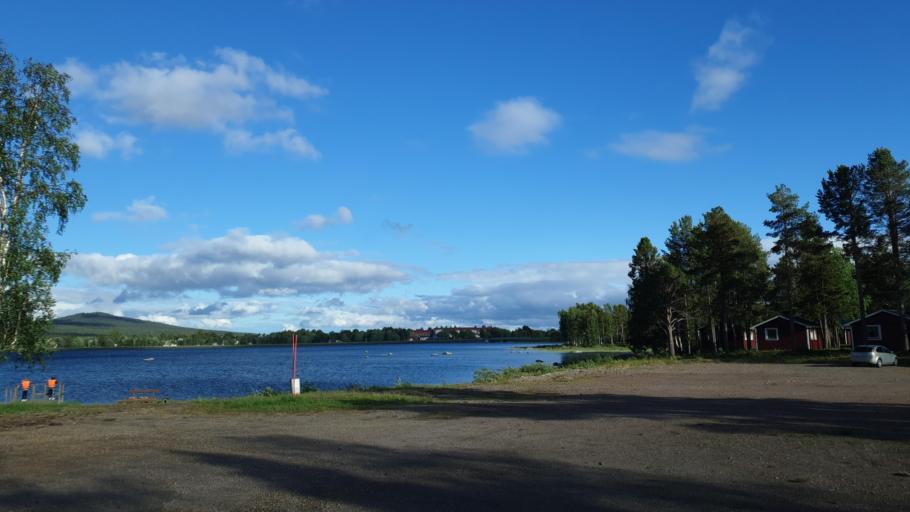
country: SE
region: Norrbotten
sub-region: Arjeplogs Kommun
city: Arjeplog
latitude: 66.0525
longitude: 17.8659
